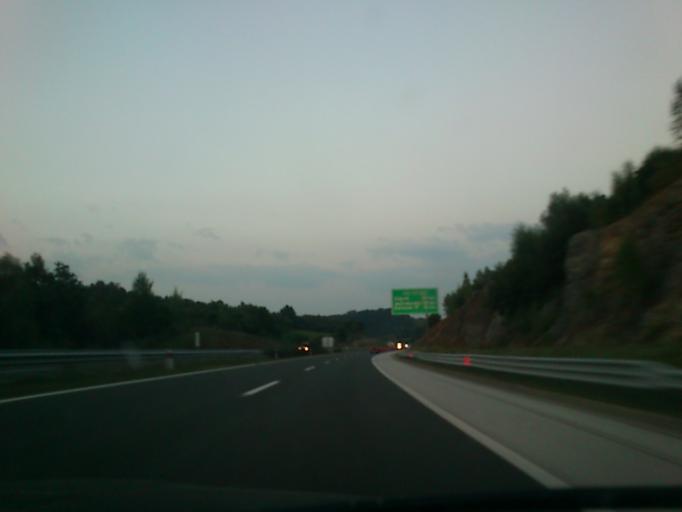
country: HR
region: Karlovacka
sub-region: Grad Karlovac
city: Karlovac
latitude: 45.4832
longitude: 15.4345
